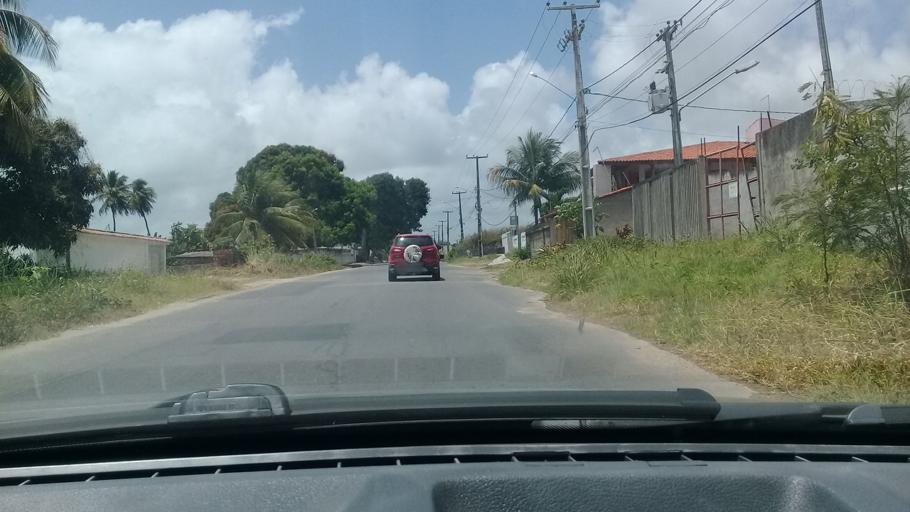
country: BR
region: Pernambuco
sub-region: Itamaraca
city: Itamaraca
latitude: -7.7787
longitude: -34.8359
